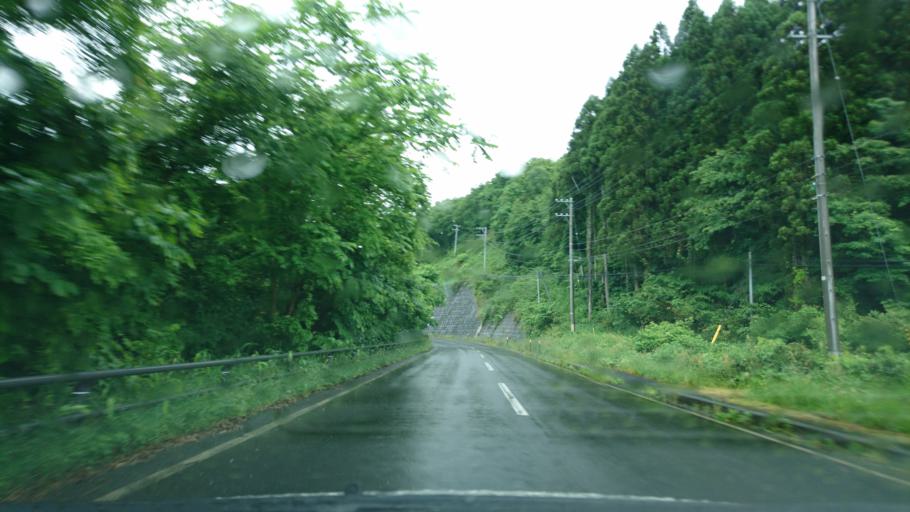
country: JP
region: Iwate
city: Ichinoseki
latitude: 38.9739
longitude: 140.9454
